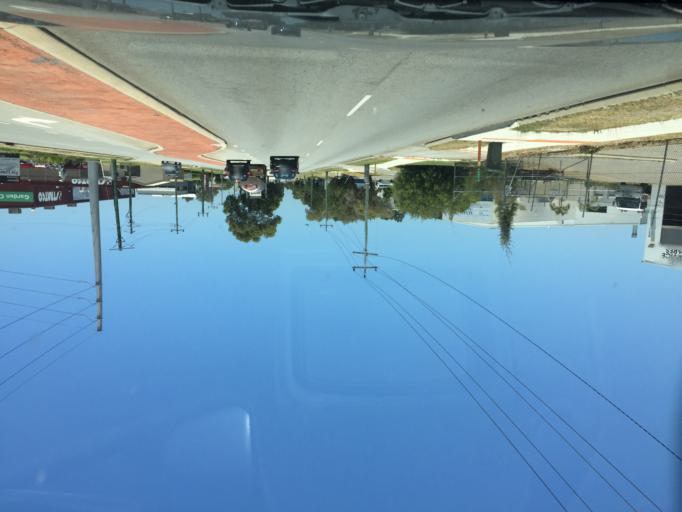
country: AU
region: Western Australia
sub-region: Canning
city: Canning Vale
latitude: -32.0610
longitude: 115.9061
